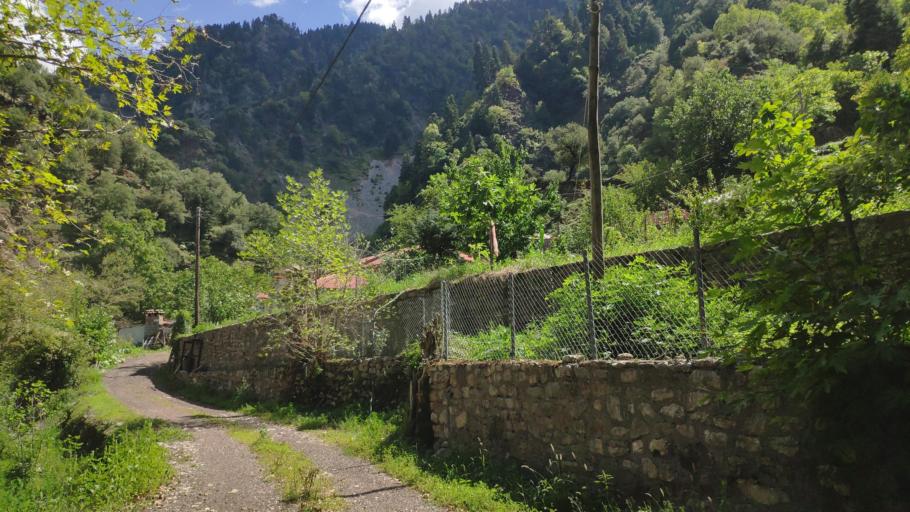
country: GR
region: Central Greece
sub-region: Nomos Evrytanias
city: Kerasochori
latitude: 39.1233
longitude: 21.6551
